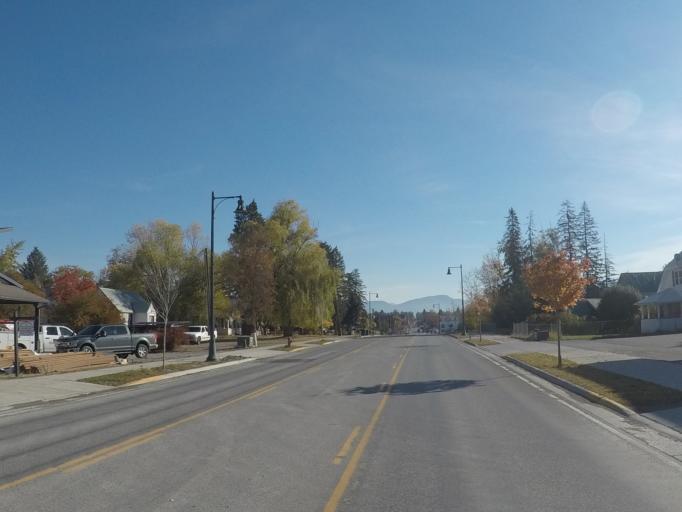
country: US
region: Montana
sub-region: Flathead County
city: Whitefish
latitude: 48.4106
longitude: -114.3468
